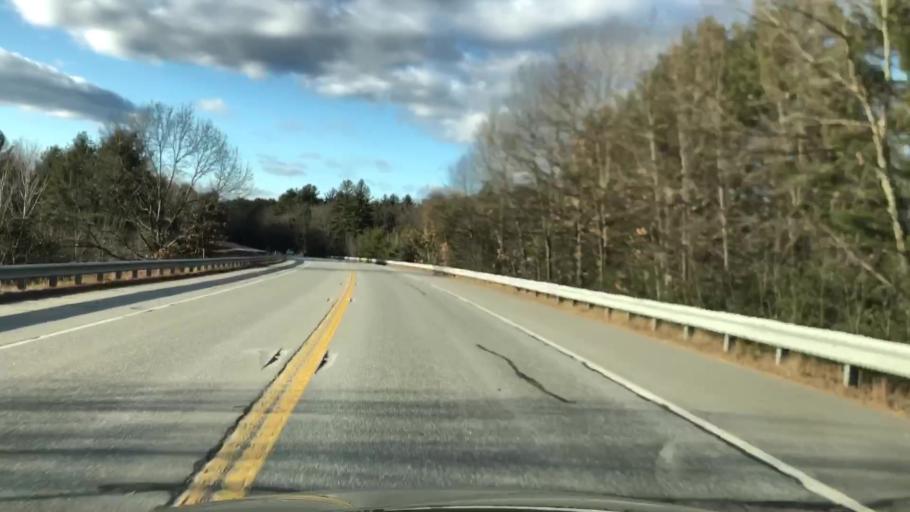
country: US
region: New Hampshire
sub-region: Hillsborough County
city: Milford
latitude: 42.8248
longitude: -71.6624
